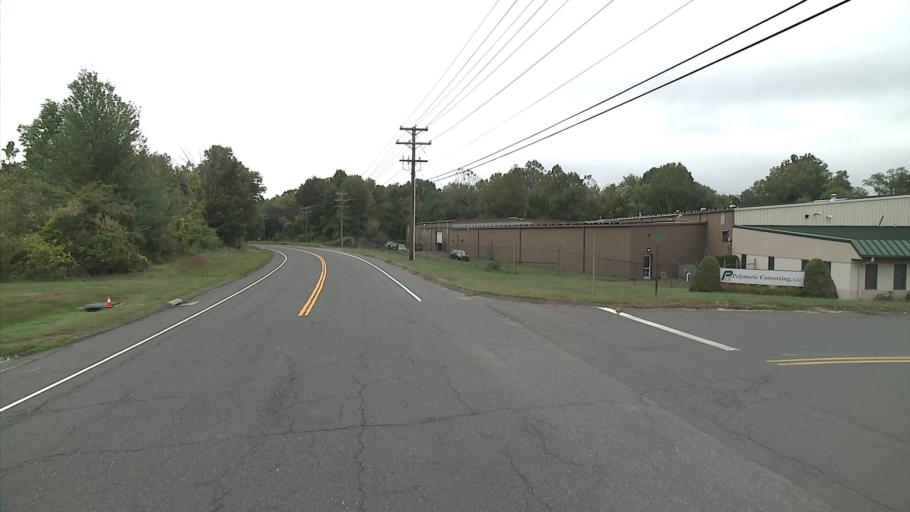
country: US
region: Connecticut
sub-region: Hartford County
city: Windsor Locks
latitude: 41.9428
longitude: -72.6093
